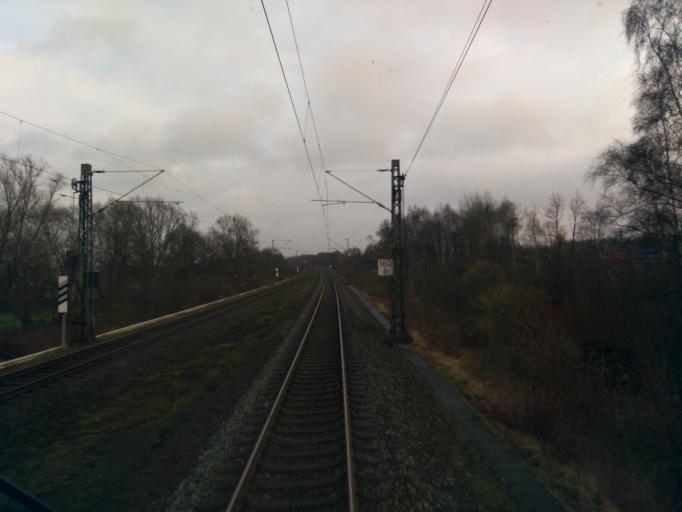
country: DE
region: Lower Saxony
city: Stelle
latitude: 53.3980
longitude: 10.0766
